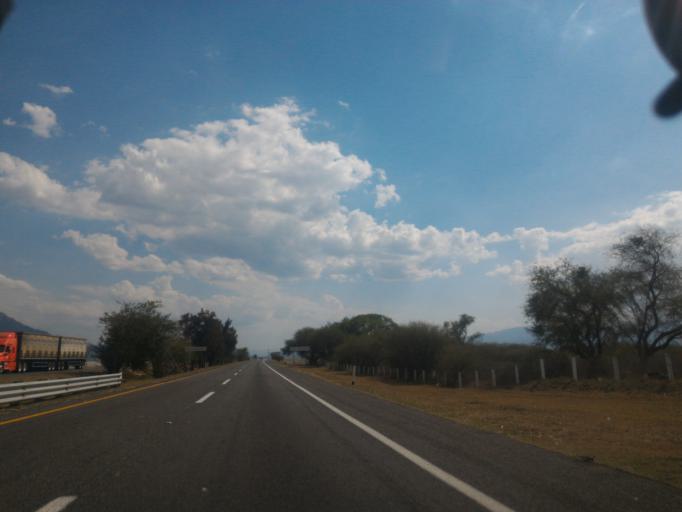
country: MX
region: Jalisco
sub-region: Acatlan de Juarez
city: Villa de los Ninos
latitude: 20.3305
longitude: -103.5687
